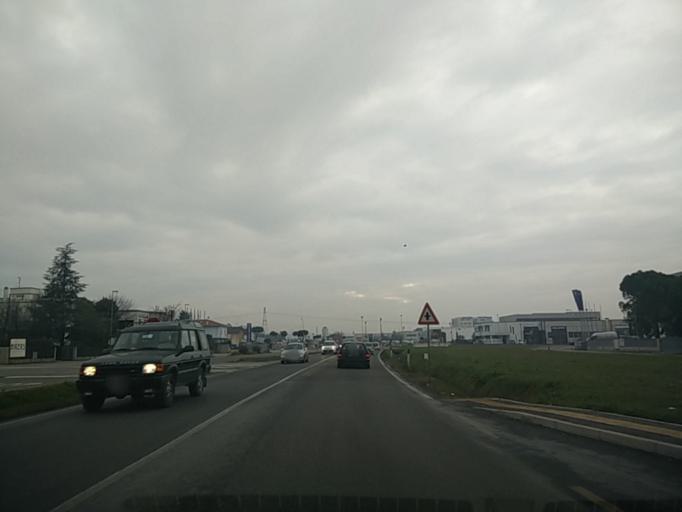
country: IT
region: Emilia-Romagna
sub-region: Provincia di Rimini
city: Santa Giustina
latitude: 44.0675
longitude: 12.4713
